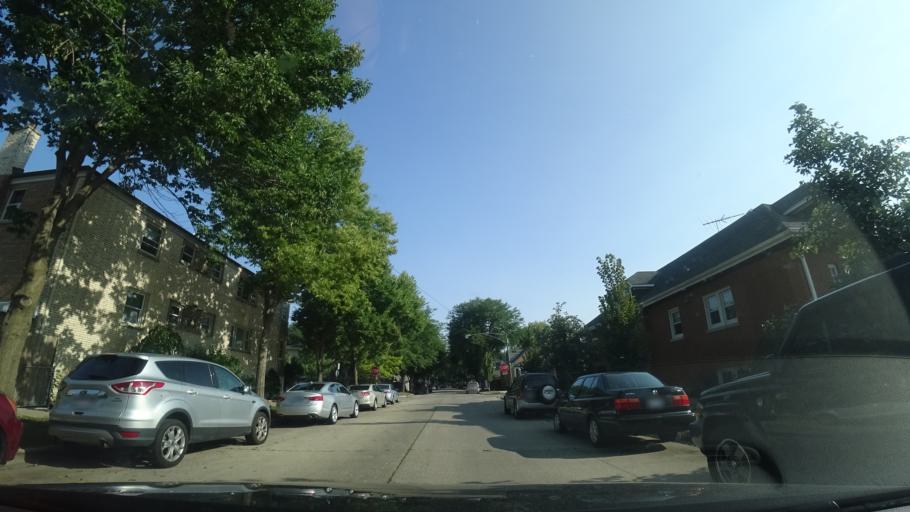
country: US
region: Illinois
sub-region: Cook County
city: Harwood Heights
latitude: 41.9641
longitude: -87.7649
